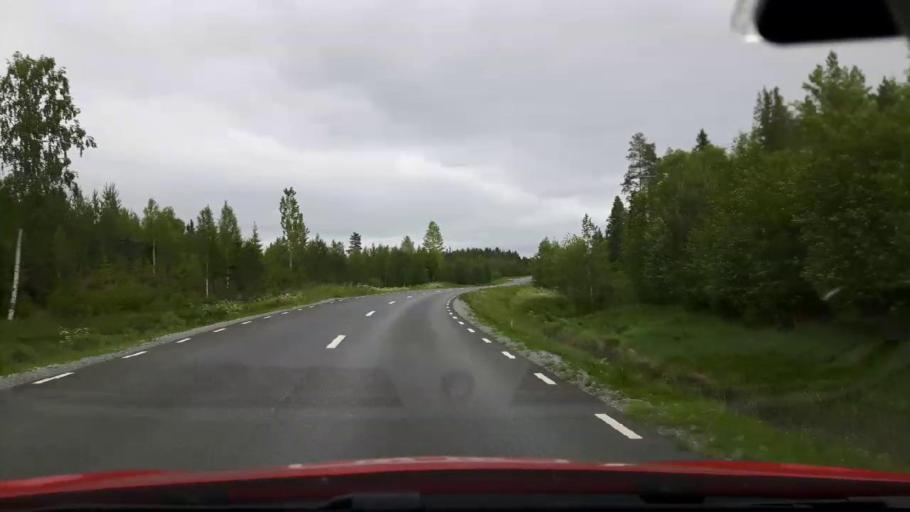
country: SE
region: Jaemtland
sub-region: OEstersunds Kommun
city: Lit
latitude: 63.7380
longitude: 14.7638
